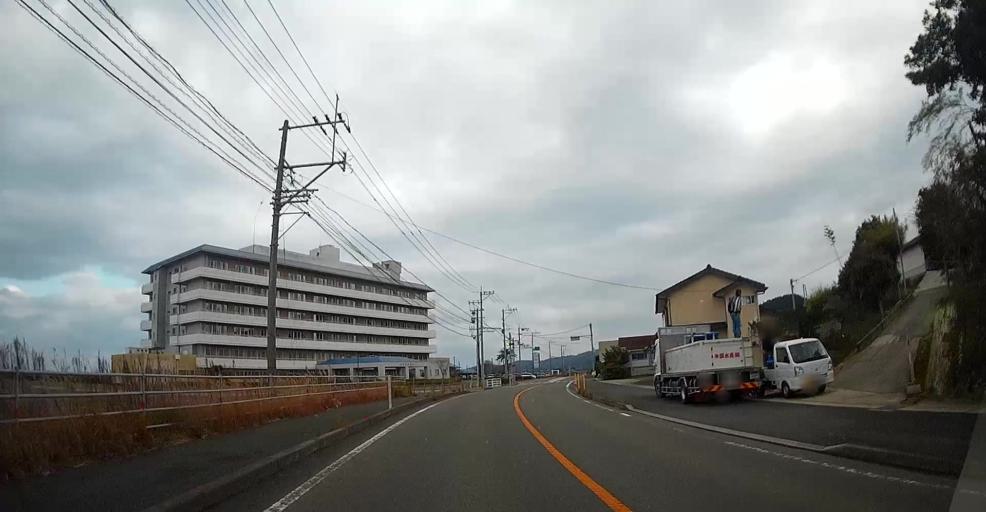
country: JP
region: Kumamoto
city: Hondo
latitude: 32.4820
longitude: 130.2737
